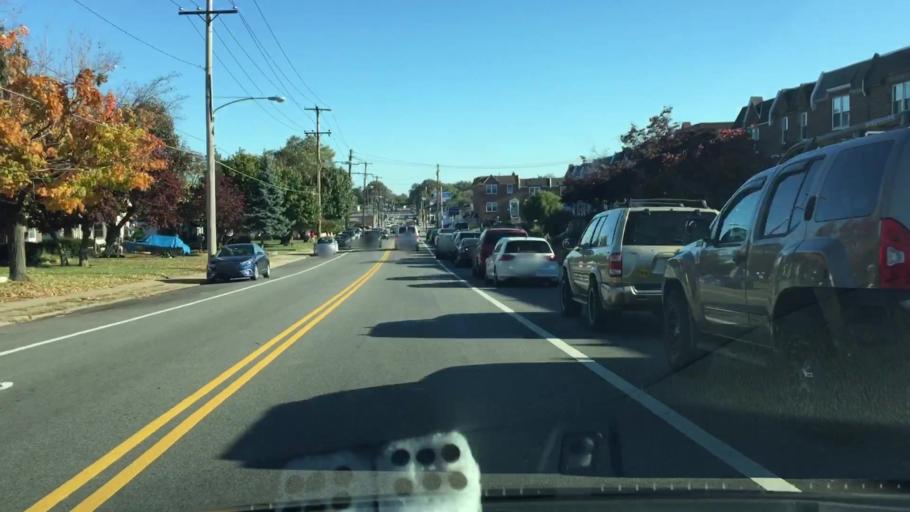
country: US
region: New Jersey
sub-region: Burlington County
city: Riverton
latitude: 40.0590
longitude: -75.0170
